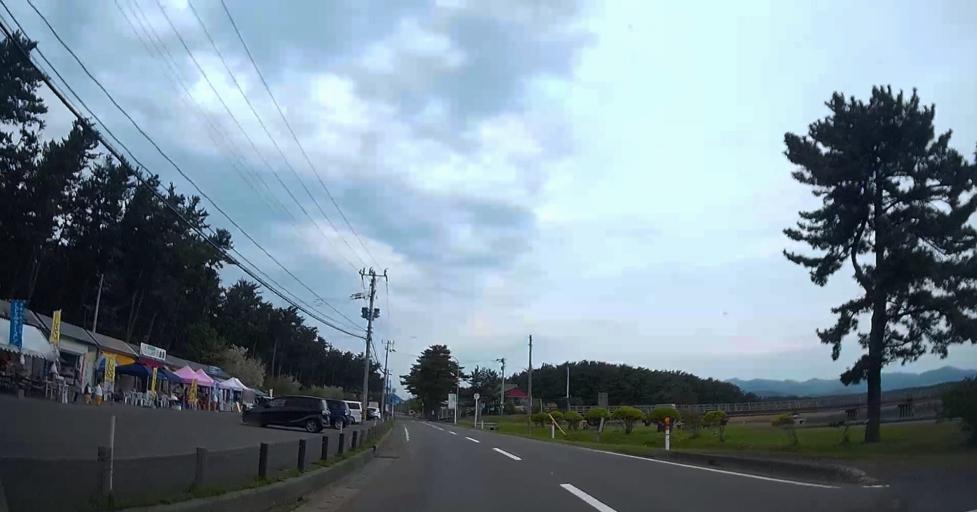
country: JP
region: Aomori
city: Shimokizukuri
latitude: 41.0469
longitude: 140.3290
